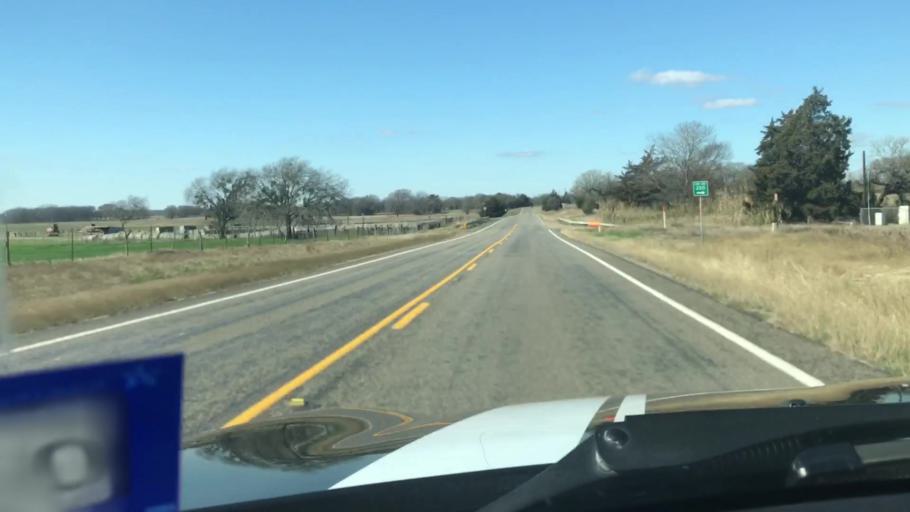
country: US
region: Texas
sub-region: Robertson County
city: Calvert
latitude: 30.8757
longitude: -96.7272
